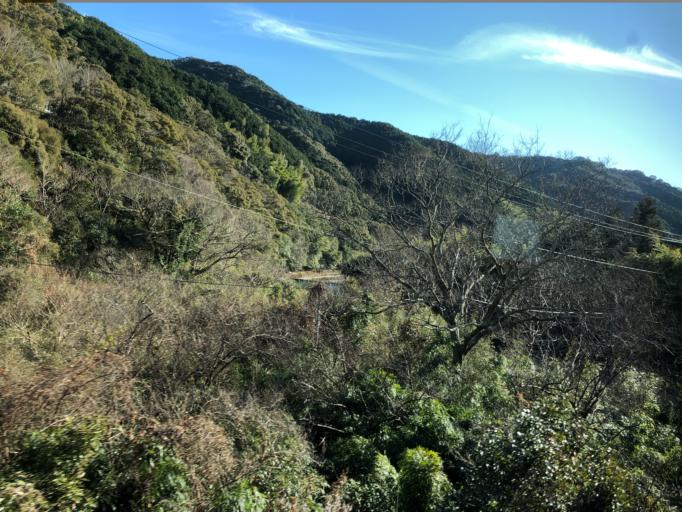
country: JP
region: Kochi
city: Nakamura
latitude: 33.1157
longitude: 133.1126
